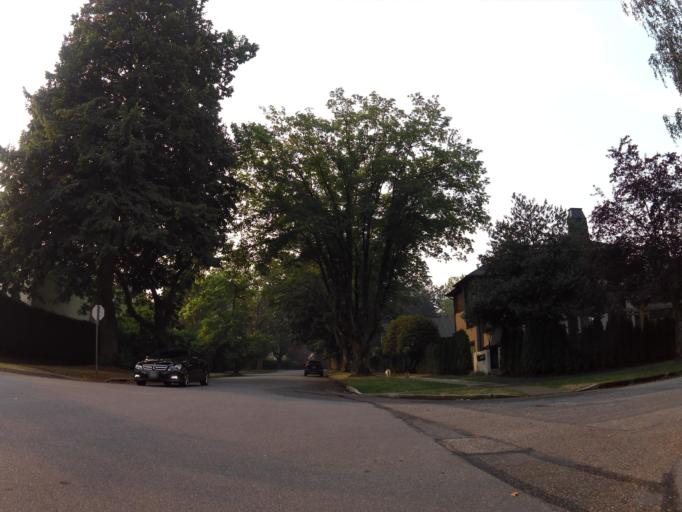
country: CA
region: British Columbia
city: Vancouver
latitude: 49.2401
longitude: -123.1457
